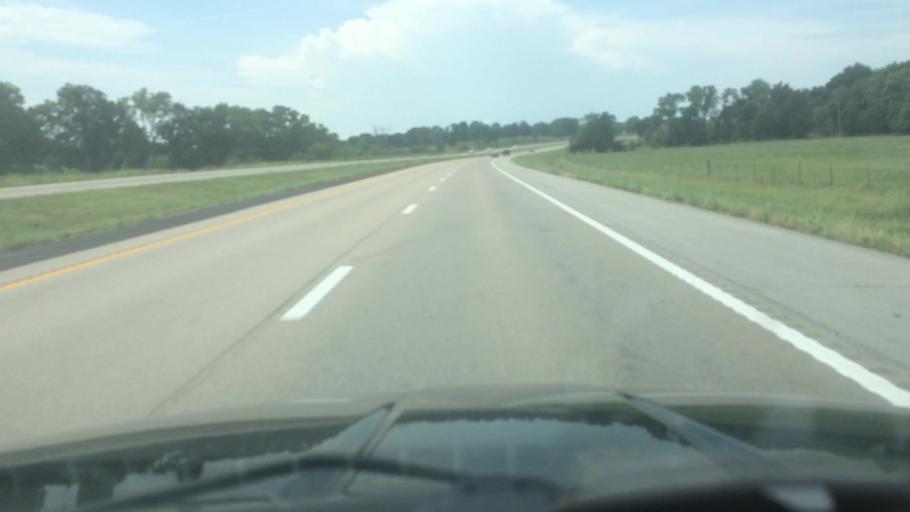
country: US
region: Missouri
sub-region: Polk County
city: Humansville
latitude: 37.8192
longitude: -93.6130
